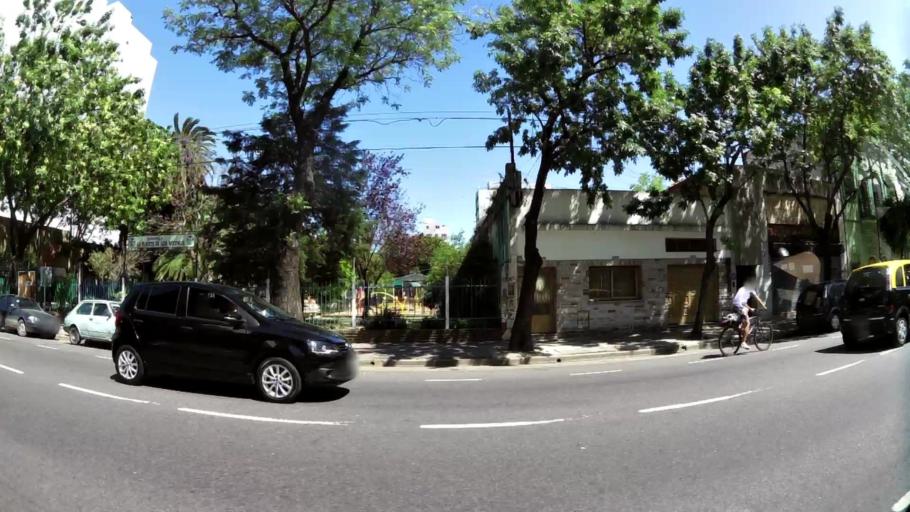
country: AR
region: Buenos Aires F.D.
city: Buenos Aires
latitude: -34.6218
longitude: -58.4263
